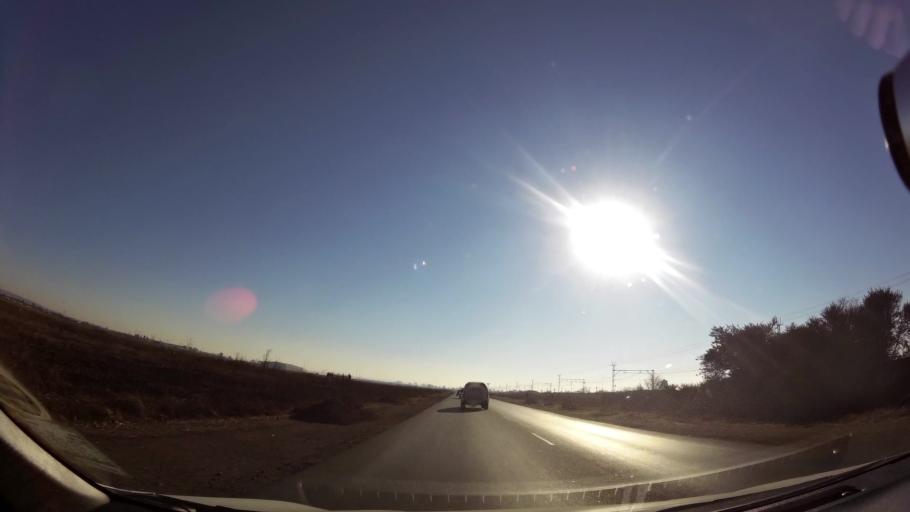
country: ZA
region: Gauteng
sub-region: Ekurhuleni Metropolitan Municipality
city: Germiston
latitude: -26.3396
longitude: 28.1330
